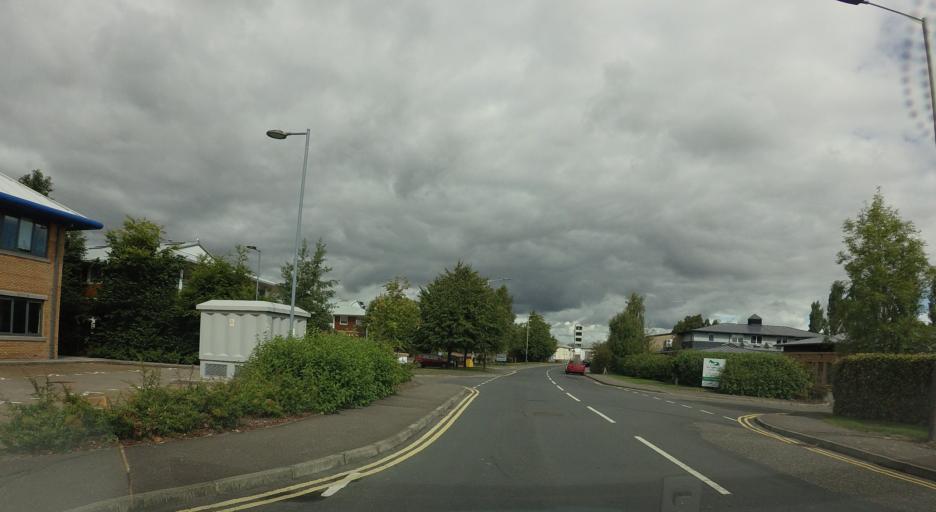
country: GB
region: Scotland
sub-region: Perth and Kinross
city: Perth
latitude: 56.3968
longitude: -3.4436
